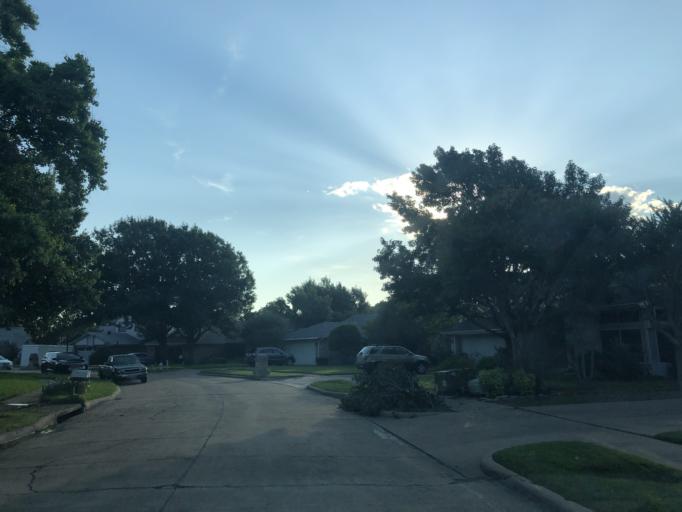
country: US
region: Texas
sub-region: Dallas County
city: Sunnyvale
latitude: 32.8409
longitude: -96.6071
